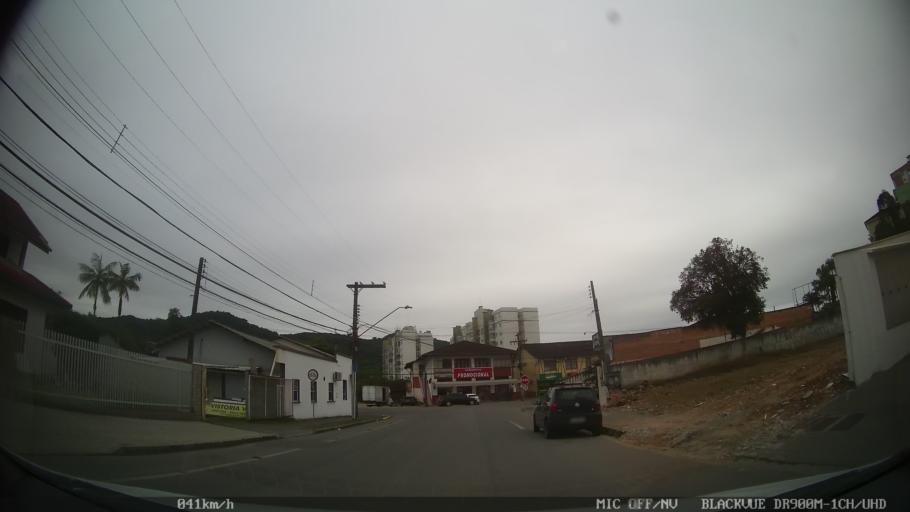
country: BR
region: Santa Catarina
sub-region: Joinville
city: Joinville
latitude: -26.2810
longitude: -48.8384
